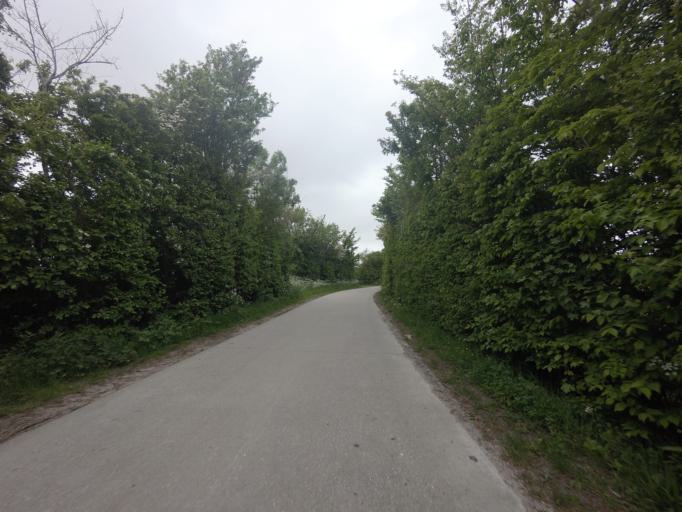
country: NL
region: Zeeland
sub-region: Gemeente Middelburg
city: Middelburg
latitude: 51.5415
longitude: 3.5815
